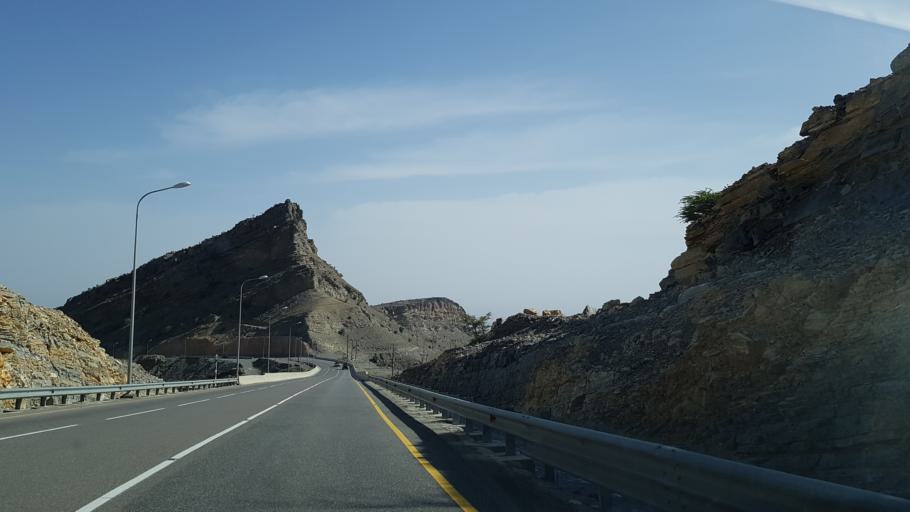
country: OM
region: Muhafazat ad Dakhiliyah
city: Izki
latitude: 23.0181
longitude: 57.6951
